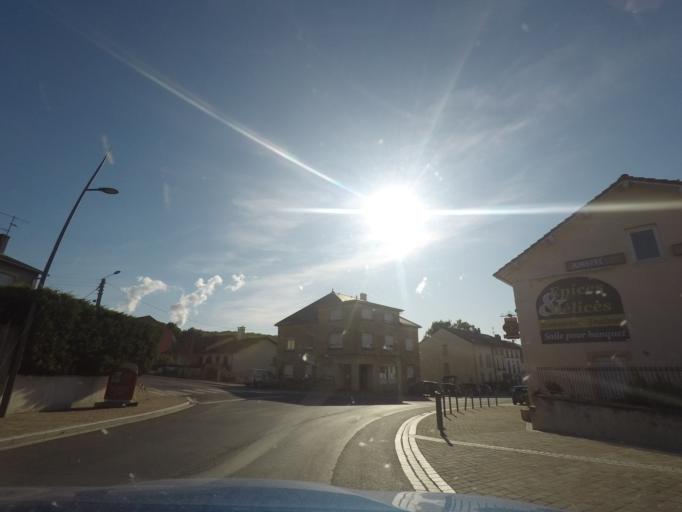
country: FR
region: Lorraine
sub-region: Departement de la Moselle
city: Hettange-Grande
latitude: 49.4071
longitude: 6.1541
